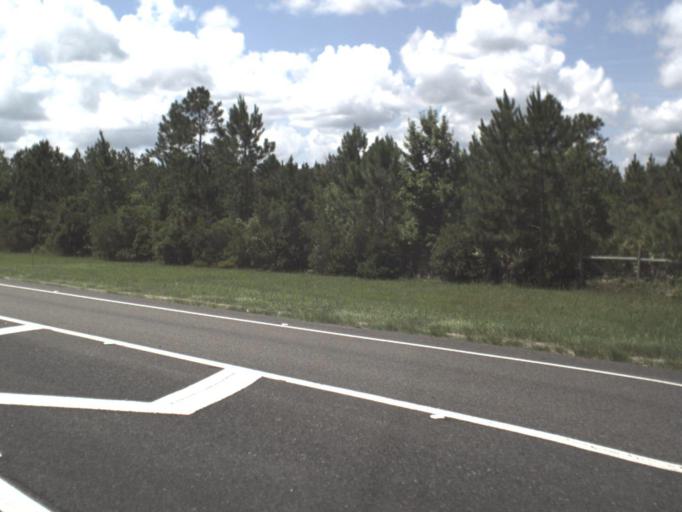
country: US
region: Florida
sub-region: Saint Johns County
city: Saint Augustine Shores
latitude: 29.7446
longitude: -81.3454
